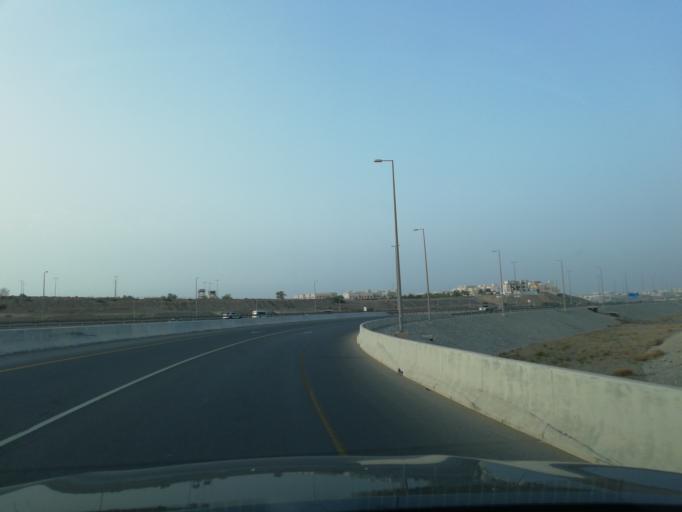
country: OM
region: Muhafazat Masqat
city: Bawshar
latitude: 23.5722
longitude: 58.4298
